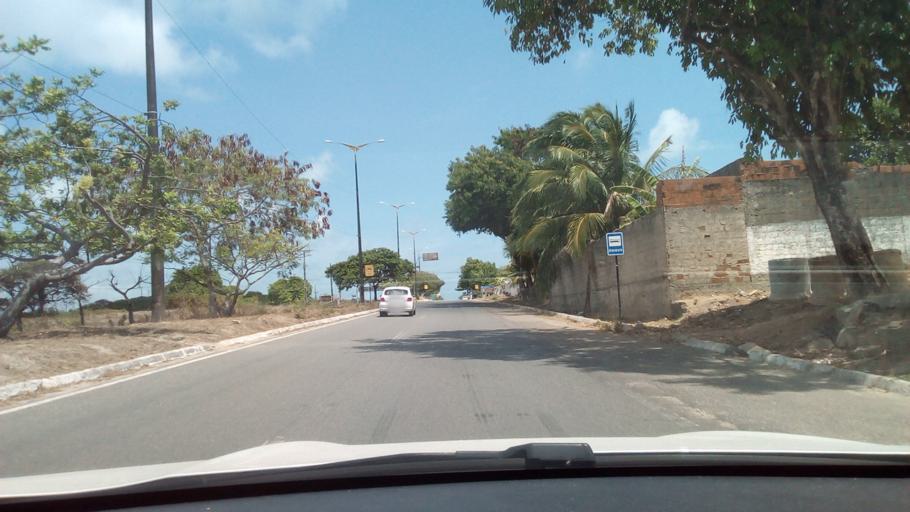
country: BR
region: Paraiba
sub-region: Joao Pessoa
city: Joao Pessoa
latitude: -7.1648
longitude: -34.8007
